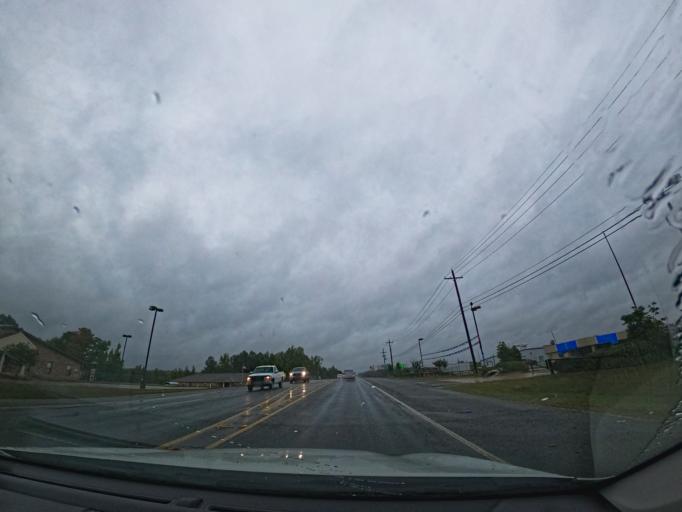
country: US
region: Louisiana
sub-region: Webster Parish
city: Minden
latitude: 32.6259
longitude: -93.2497
